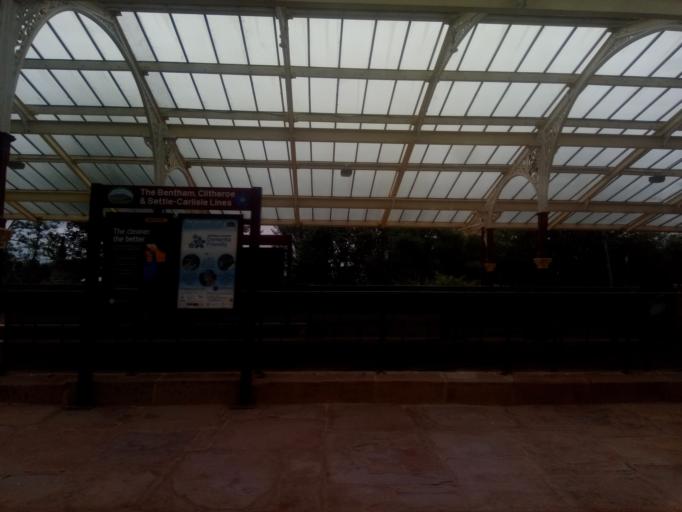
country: GB
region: England
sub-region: North Yorkshire
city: Settle
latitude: 54.0109
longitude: -2.2276
